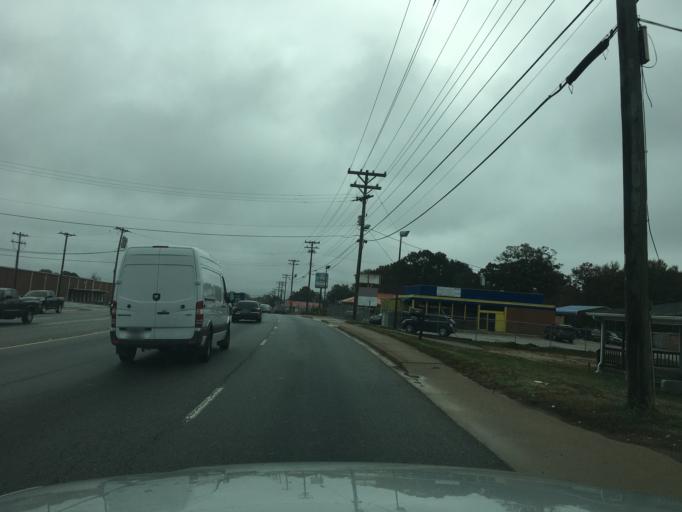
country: US
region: South Carolina
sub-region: Greenville County
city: Welcome
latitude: 34.8122
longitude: -82.4398
